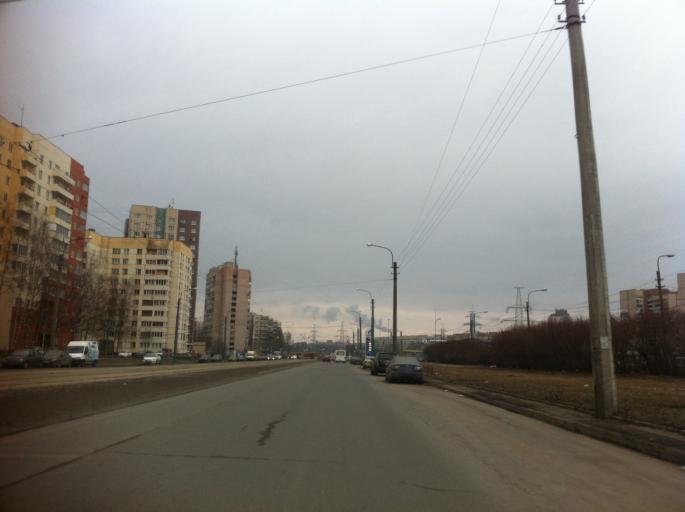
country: RU
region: St.-Petersburg
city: Uritsk
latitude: 59.8547
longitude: 30.2012
